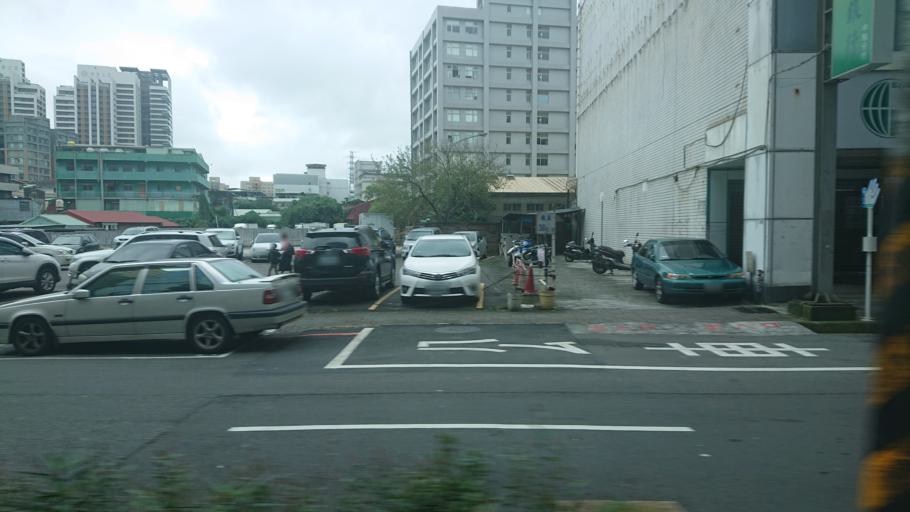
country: TW
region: Taipei
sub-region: Taipei
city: Banqiao
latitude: 24.9972
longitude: 121.4882
